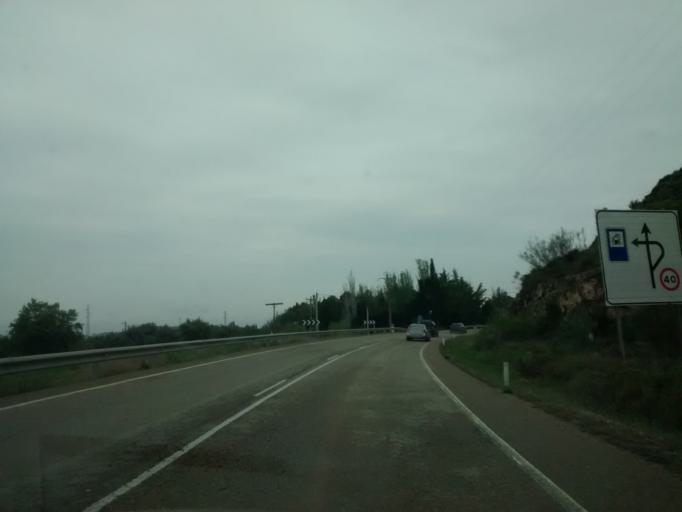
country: ES
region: Aragon
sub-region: Provincia de Zaragoza
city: Caspe
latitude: 41.2514
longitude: -0.0693
